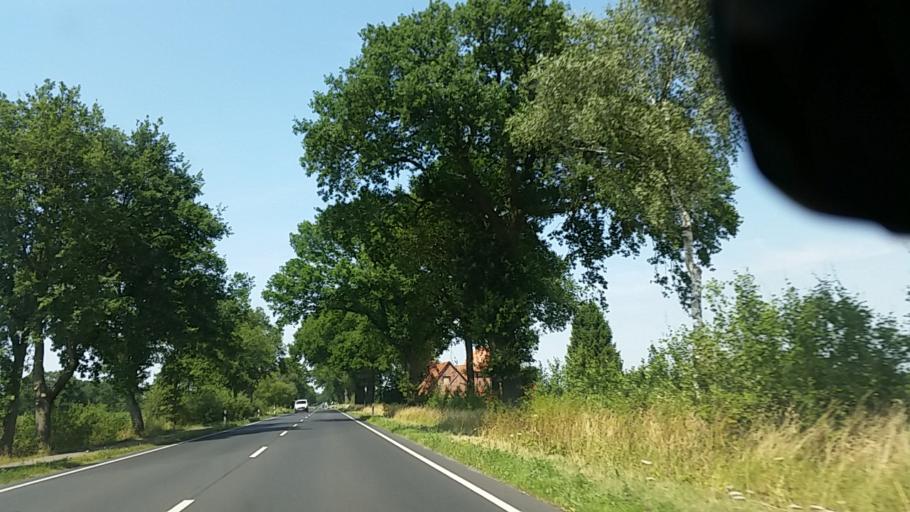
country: DE
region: Lower Saxony
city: Wietzen
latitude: 52.6944
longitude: 9.0896
